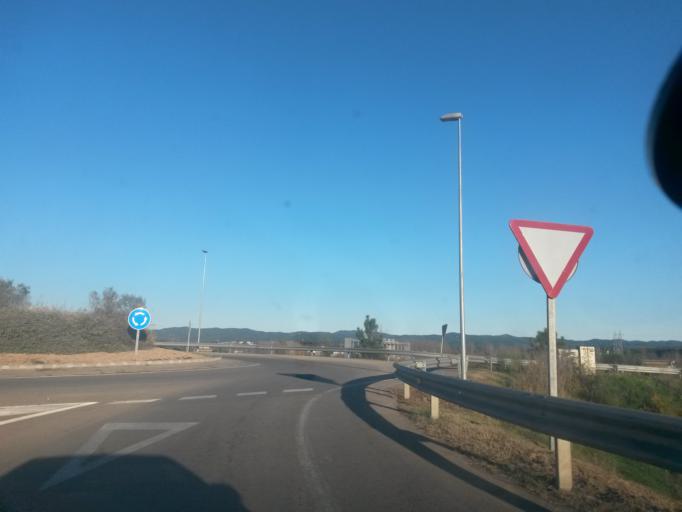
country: ES
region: Catalonia
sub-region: Provincia de Girona
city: Vilablareix
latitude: 41.9429
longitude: 2.7877
